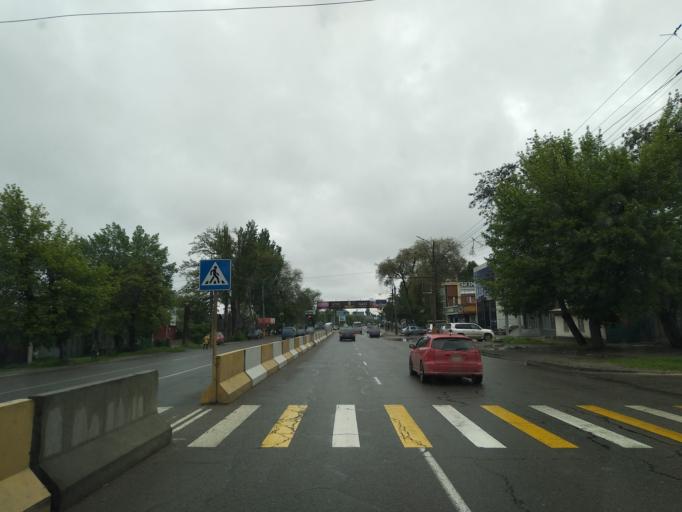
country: KG
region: Chuy
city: Lebedinovka
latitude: 42.8886
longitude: 74.6543
